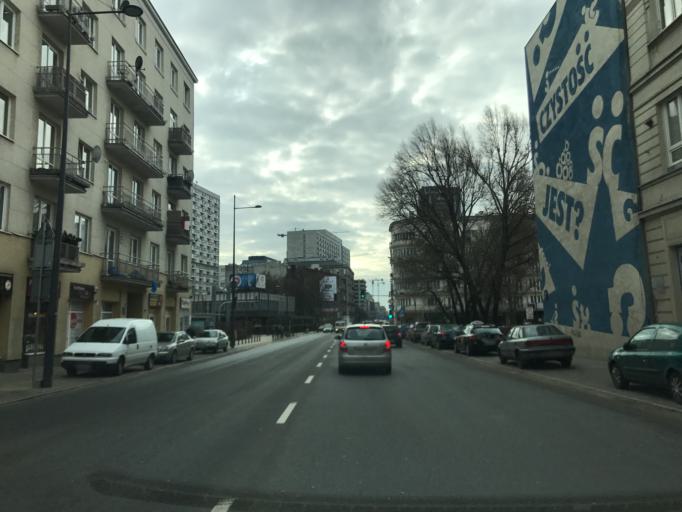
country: PL
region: Masovian Voivodeship
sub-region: Warszawa
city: Wola
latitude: 52.2381
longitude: 20.9884
